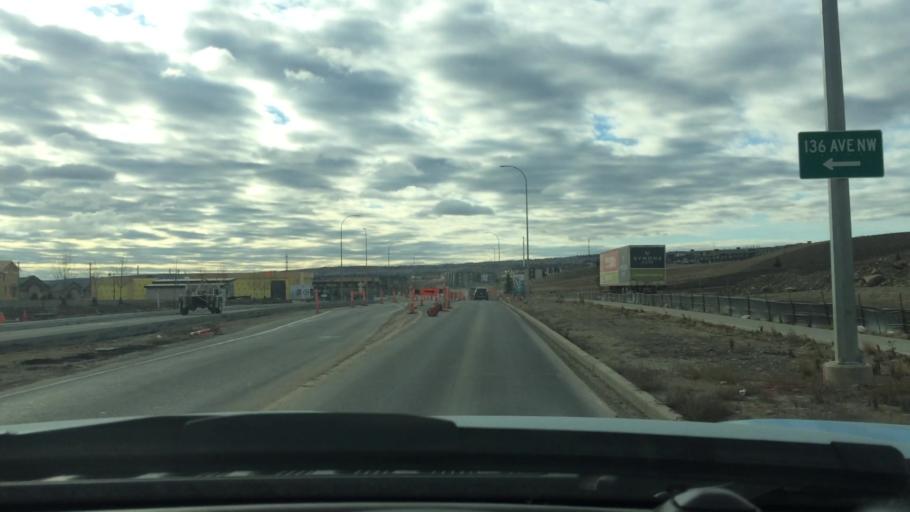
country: CA
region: Alberta
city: Calgary
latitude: 51.1774
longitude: -114.1336
